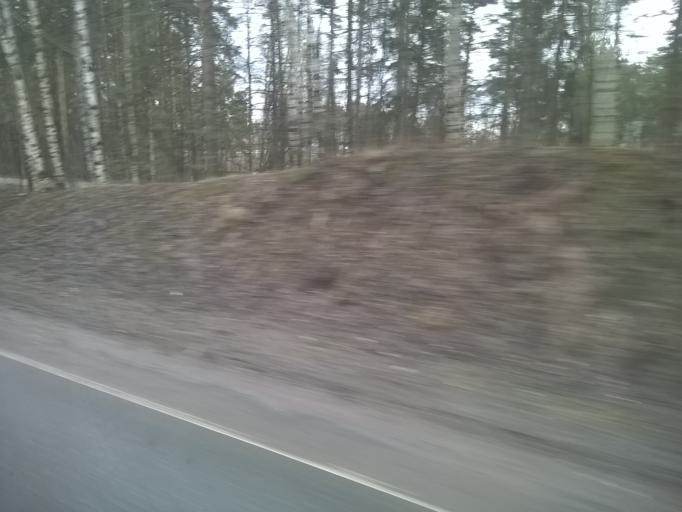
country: FI
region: Pirkanmaa
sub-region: Tampere
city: Tampere
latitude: 61.4667
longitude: 23.8421
